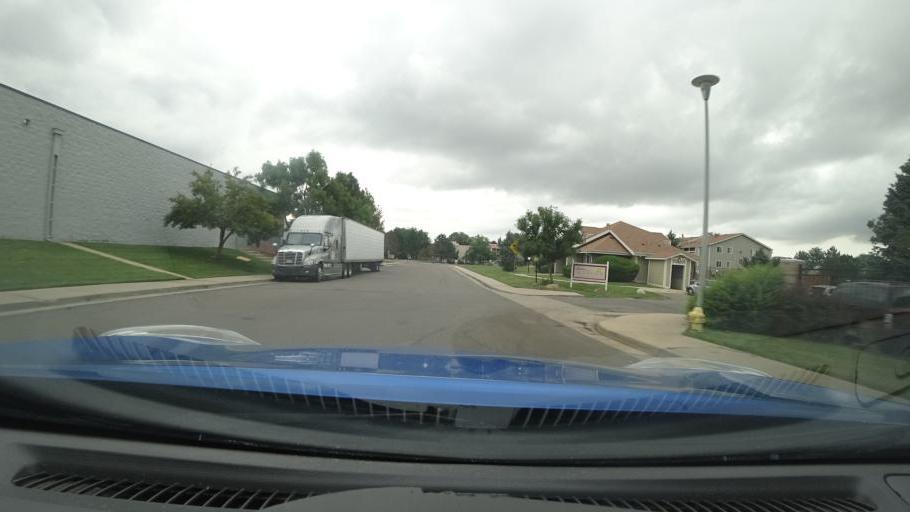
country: US
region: Colorado
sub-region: Adams County
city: Aurora
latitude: 39.6974
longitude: -104.8167
